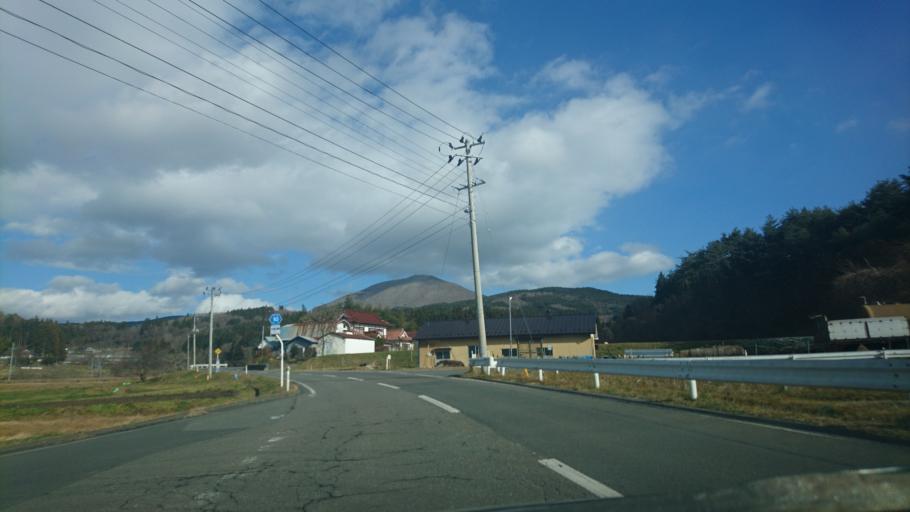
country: JP
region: Iwate
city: Ichinoseki
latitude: 38.9523
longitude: 141.4120
